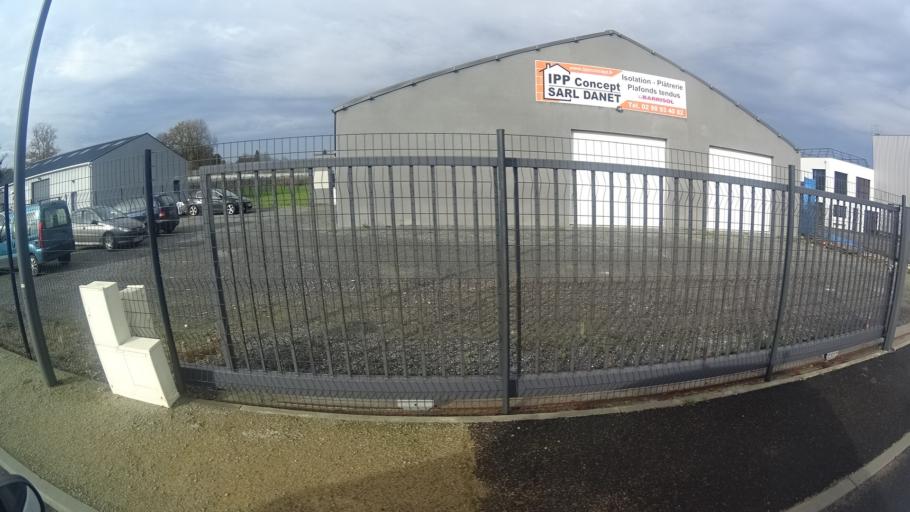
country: FR
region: Brittany
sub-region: Departement du Morbihan
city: Rieux
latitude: 47.6188
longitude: -2.1114
